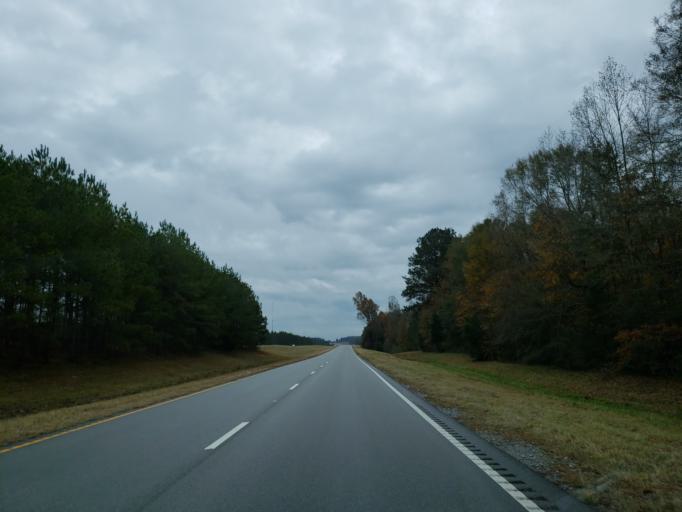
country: US
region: Mississippi
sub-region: Wayne County
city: Waynesboro
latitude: 31.6942
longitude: -88.7187
